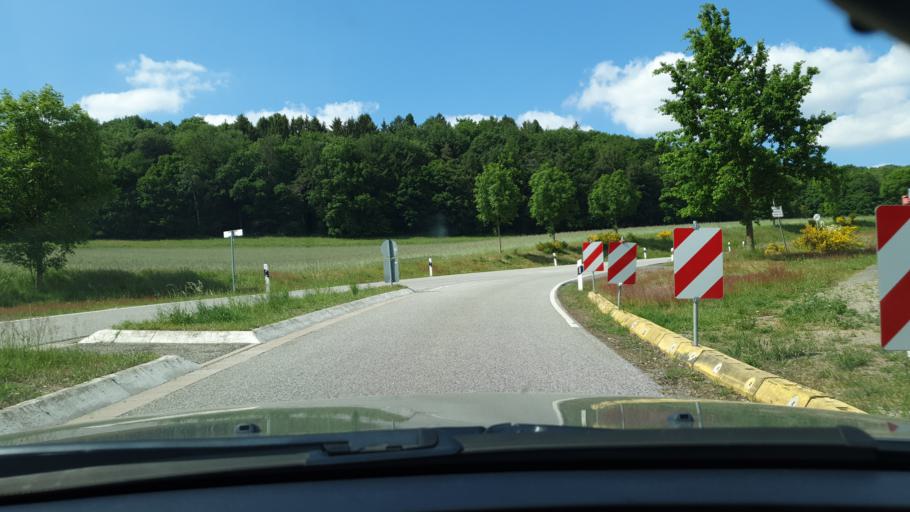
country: DE
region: Rheinland-Pfalz
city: Lambsborn
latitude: 49.3690
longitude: 7.4375
